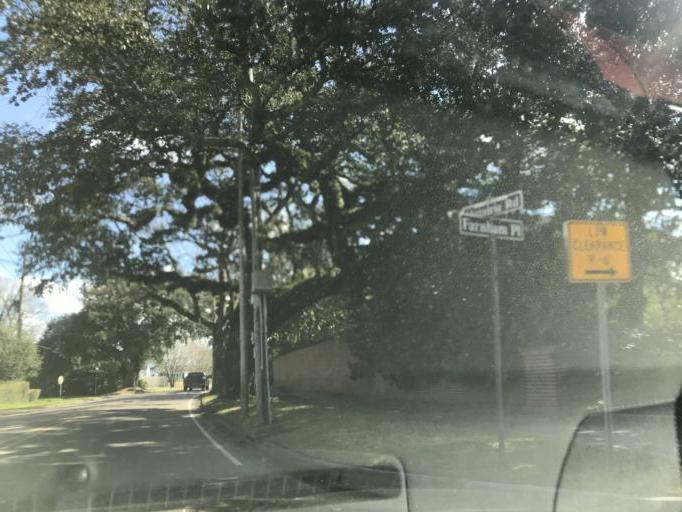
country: US
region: Louisiana
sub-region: Jefferson Parish
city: Metairie
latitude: 29.9892
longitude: -90.1349
